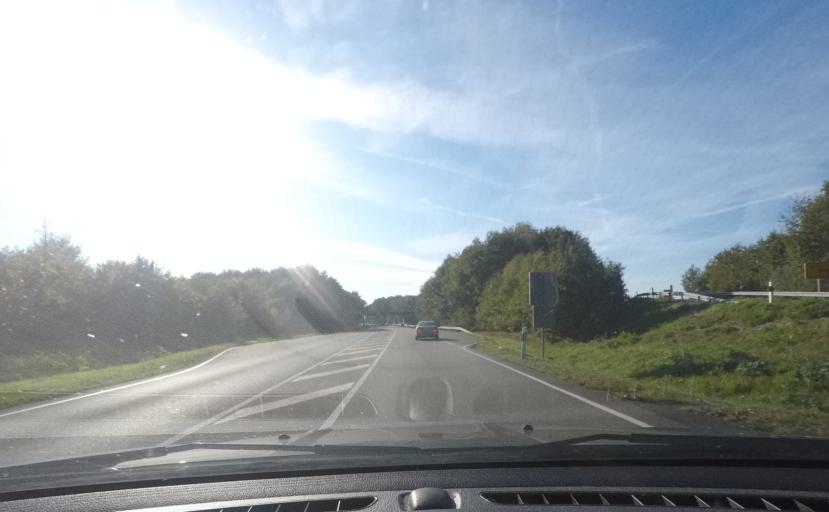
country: DE
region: North Rhine-Westphalia
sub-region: Regierungsbezirk Munster
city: Heiden
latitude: 51.8532
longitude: 6.9239
